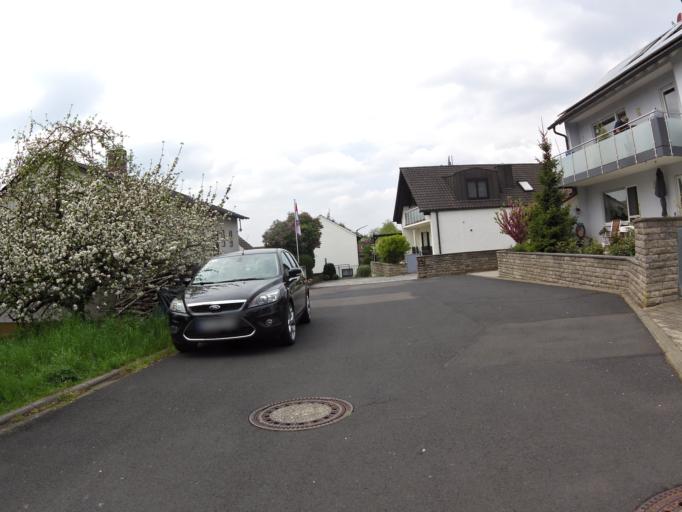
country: DE
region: Bavaria
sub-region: Regierungsbezirk Unterfranken
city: Kurnach
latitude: 49.8480
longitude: 10.0424
